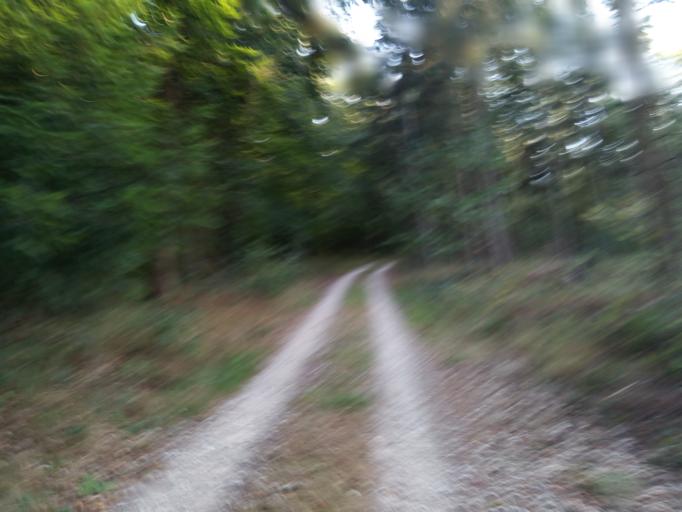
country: DE
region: Rheinland-Pfalz
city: Waldlaubersheim
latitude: 49.9174
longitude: 7.8369
